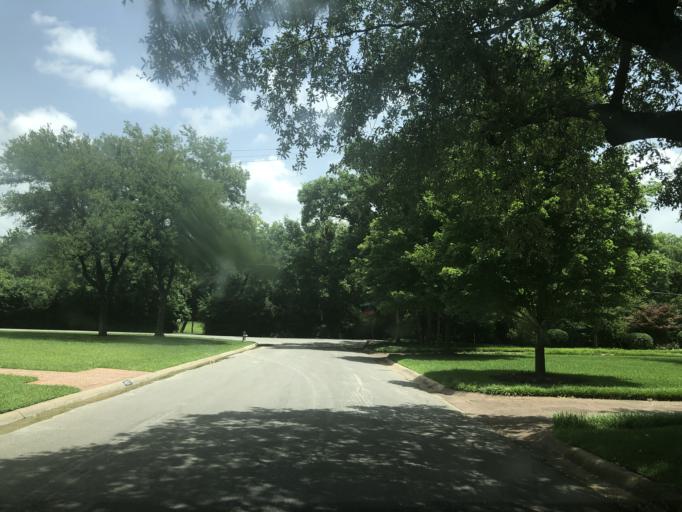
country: US
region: Texas
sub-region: Dallas County
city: University Park
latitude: 32.8725
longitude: -96.8319
